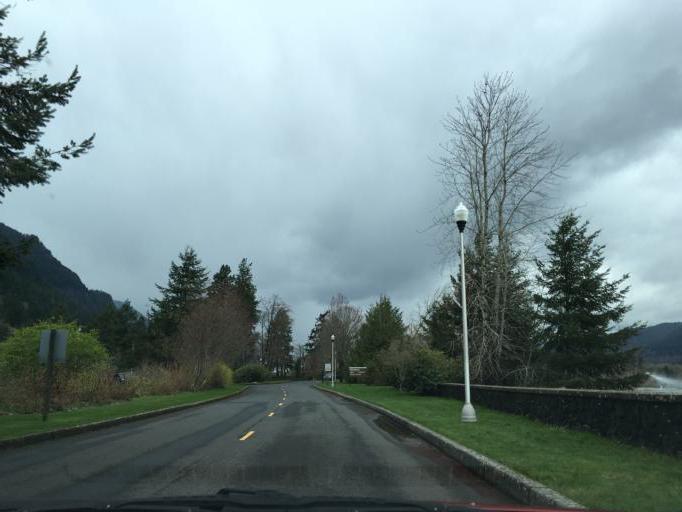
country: US
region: Oregon
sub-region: Hood River County
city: Cascade Locks
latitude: 45.6350
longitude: -121.9550
